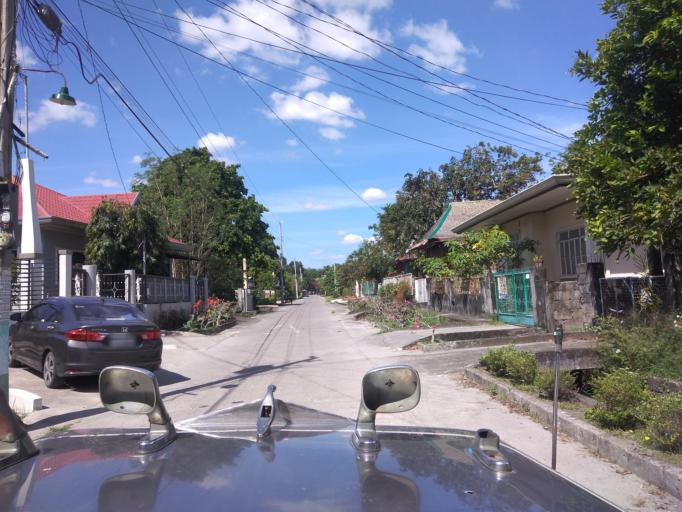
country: PH
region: Central Luzon
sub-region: Province of Pampanga
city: Santa Rita
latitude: 15.0051
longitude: 120.5972
